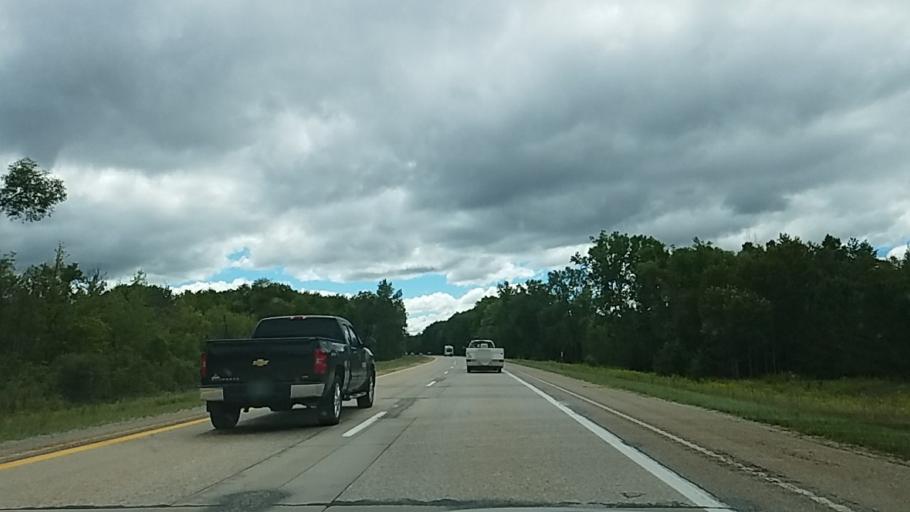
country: US
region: Michigan
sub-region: Ogemaw County
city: West Branch
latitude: 44.2232
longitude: -84.2103
